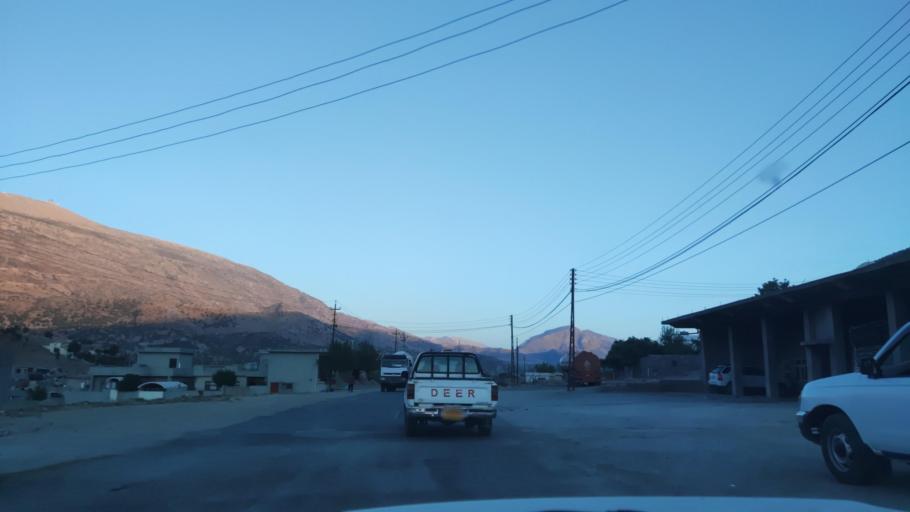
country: IQ
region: Arbil
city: Ruwandiz
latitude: 36.5884
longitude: 44.3931
